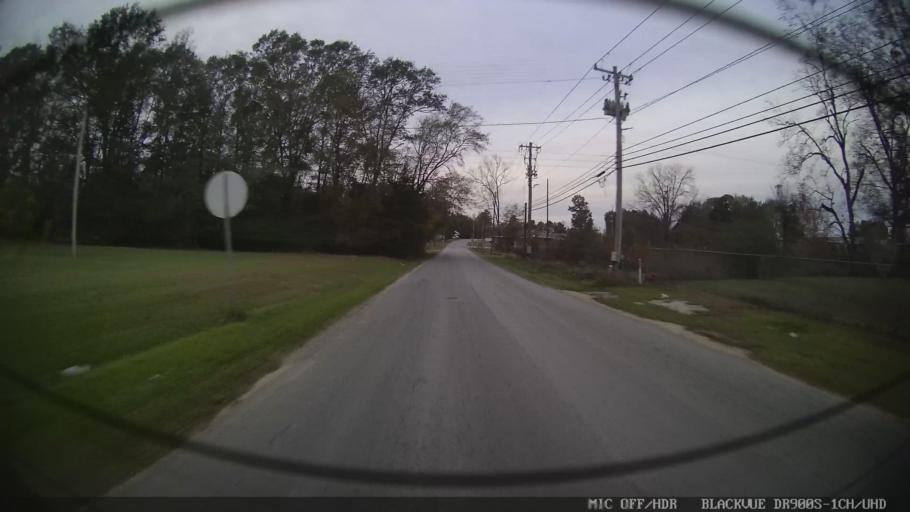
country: US
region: Mississippi
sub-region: Clarke County
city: Quitman
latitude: 32.0396
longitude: -88.7321
